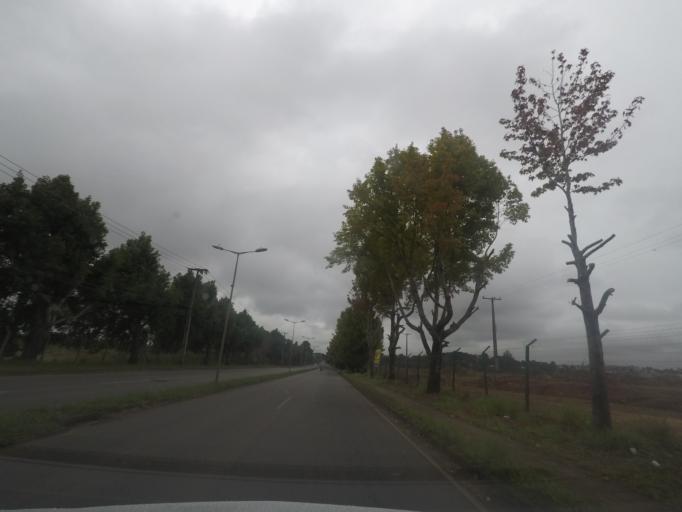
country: BR
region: Parana
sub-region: Pinhais
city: Pinhais
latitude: -25.3929
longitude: -49.1708
